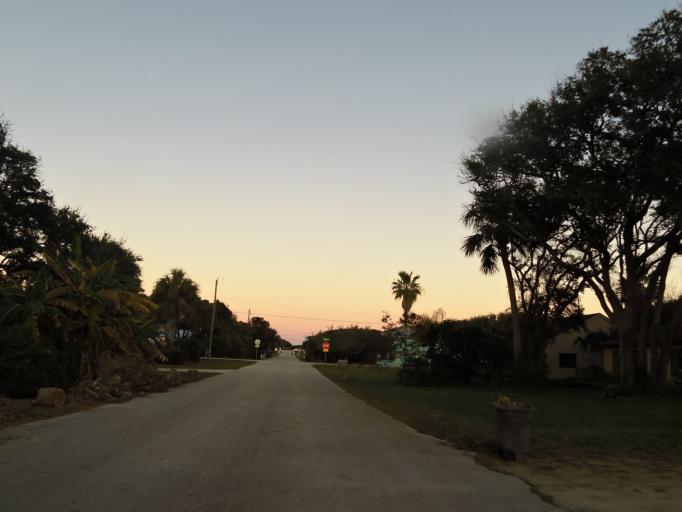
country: US
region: Florida
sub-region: Saint Johns County
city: Villano Beach
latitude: 29.9448
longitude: -81.3056
